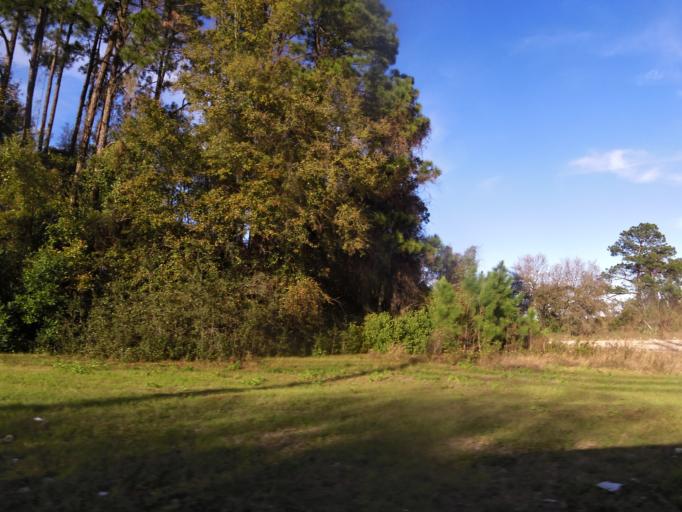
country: US
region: Florida
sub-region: Duval County
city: Jacksonville
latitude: 30.4197
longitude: -81.5995
